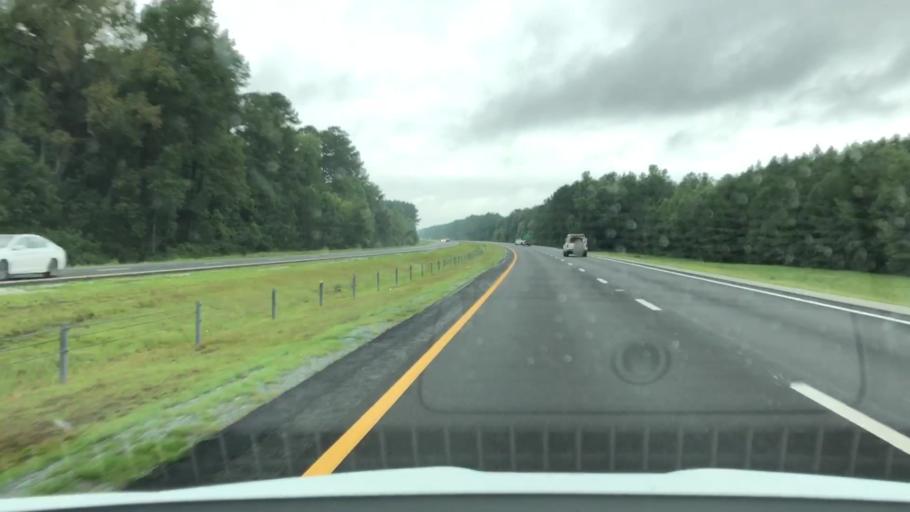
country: US
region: North Carolina
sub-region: Wayne County
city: Fremont
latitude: 35.4754
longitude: -77.9875
